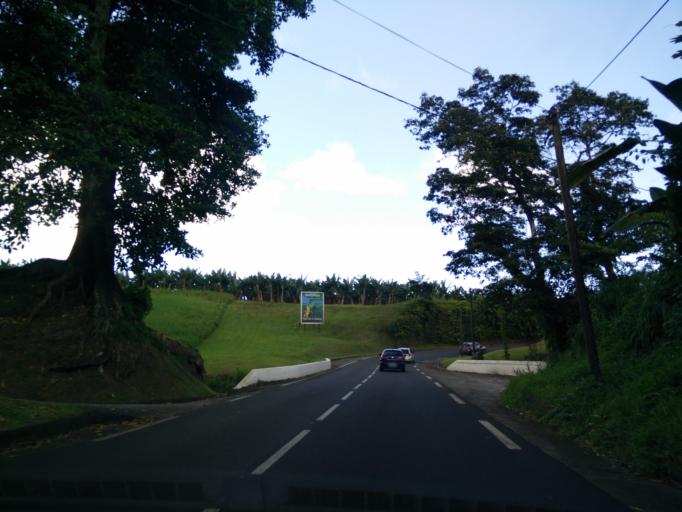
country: MQ
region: Martinique
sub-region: Martinique
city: Le Morne-Rouge
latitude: 14.8124
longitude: -61.1236
